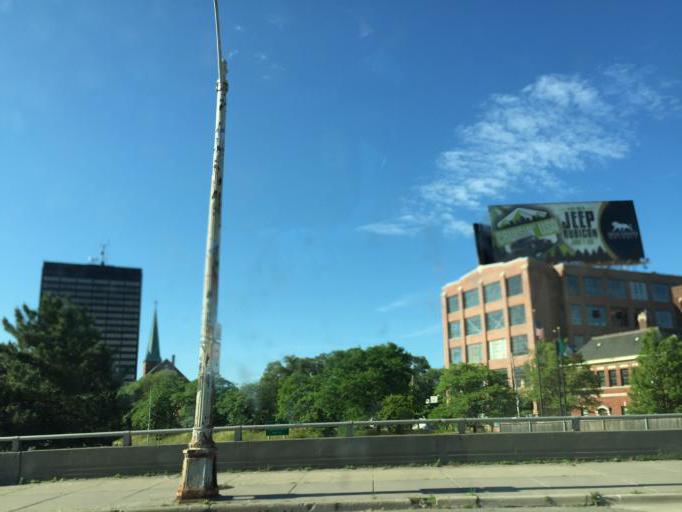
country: US
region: Michigan
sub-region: Wayne County
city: Detroit
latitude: 42.3316
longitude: -83.0615
